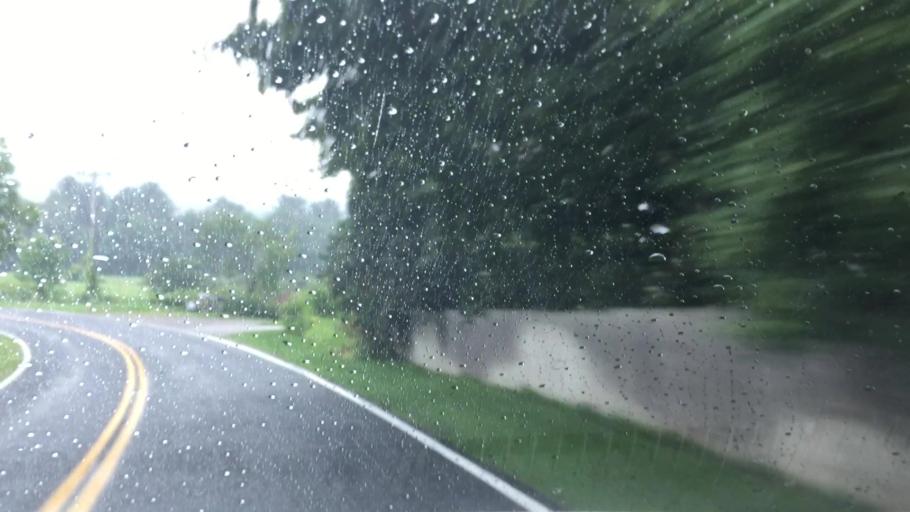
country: US
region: Massachusetts
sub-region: Berkshire County
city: Housatonic
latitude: 42.2937
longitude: -73.4029
